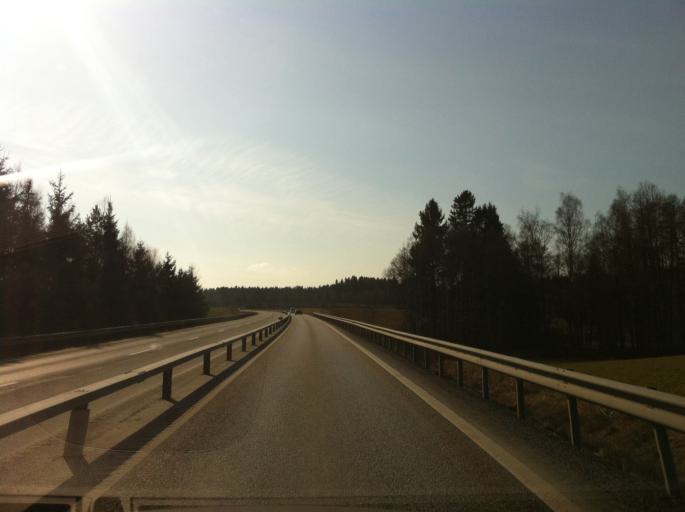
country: SE
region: Joenkoeping
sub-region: Jonkopings Kommun
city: Bankeryd
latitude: 57.8339
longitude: 14.1012
